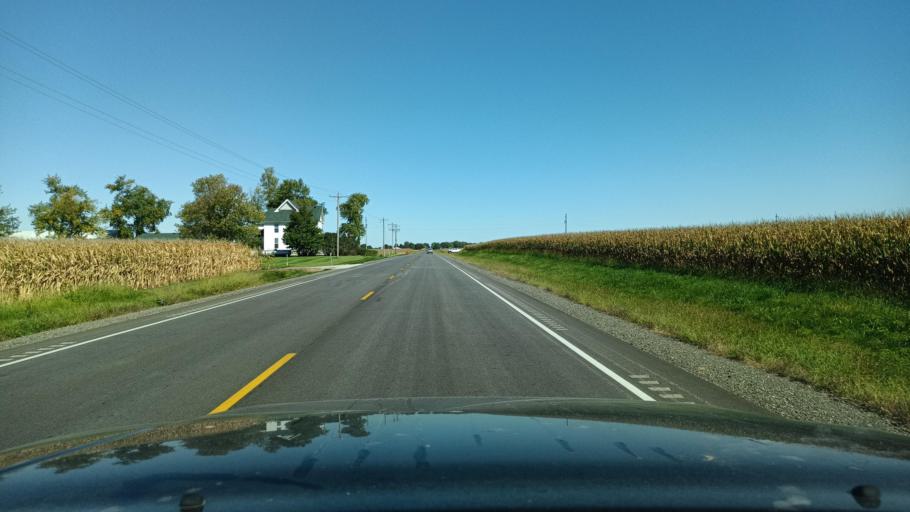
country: US
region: Illinois
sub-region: Champaign County
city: Philo
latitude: 39.9796
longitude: -88.1612
